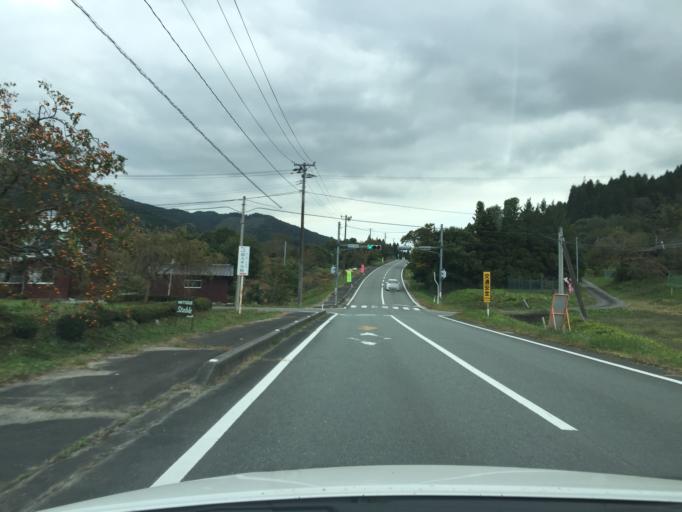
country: JP
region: Ibaraki
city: Kitaibaraki
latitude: 36.9316
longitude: 140.6889
